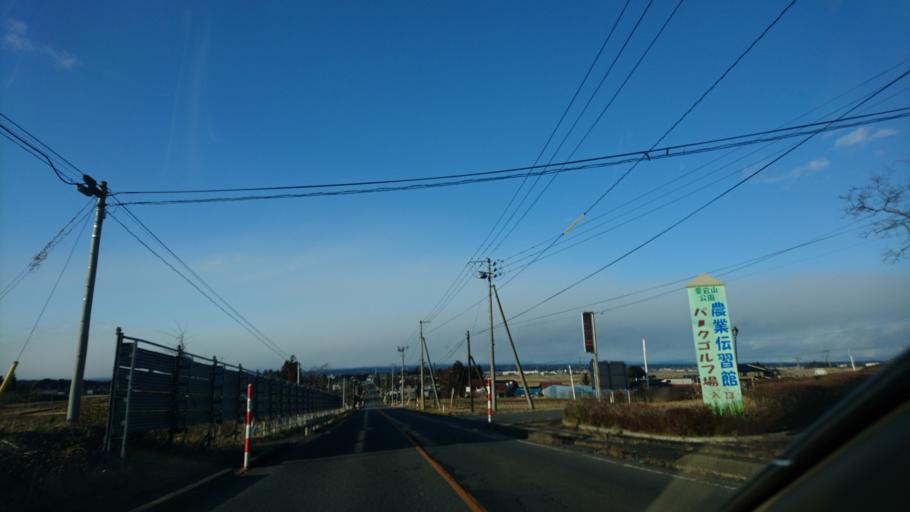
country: JP
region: Miyagi
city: Furukawa
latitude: 38.5301
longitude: 140.8593
